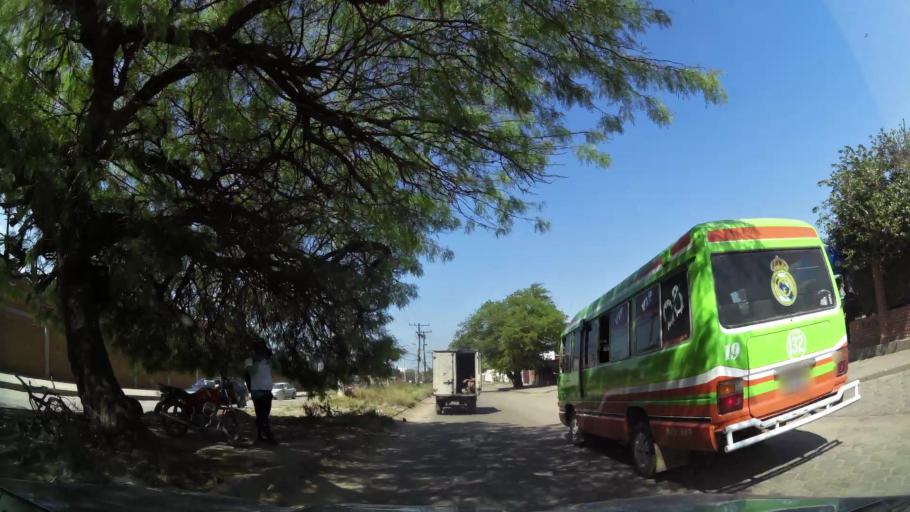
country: BO
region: Santa Cruz
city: Santa Cruz de la Sierra
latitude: -17.7586
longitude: -63.1416
